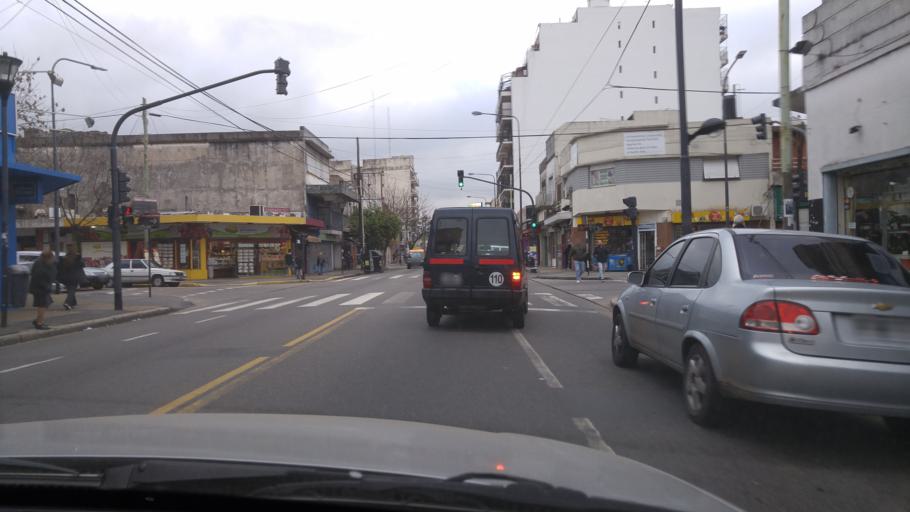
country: AR
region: Buenos Aires
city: Caseros
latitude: -34.6125
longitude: -58.5271
